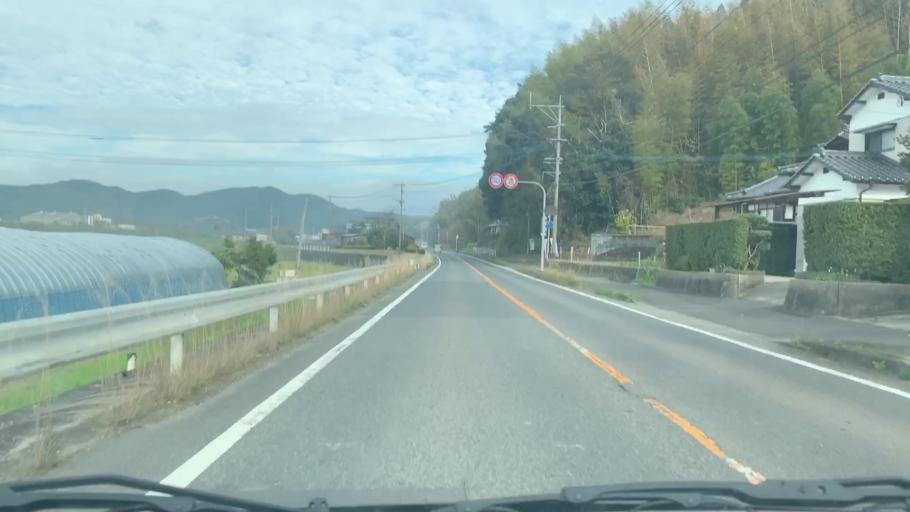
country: JP
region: Saga Prefecture
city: Karatsu
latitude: 33.3902
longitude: 129.9875
